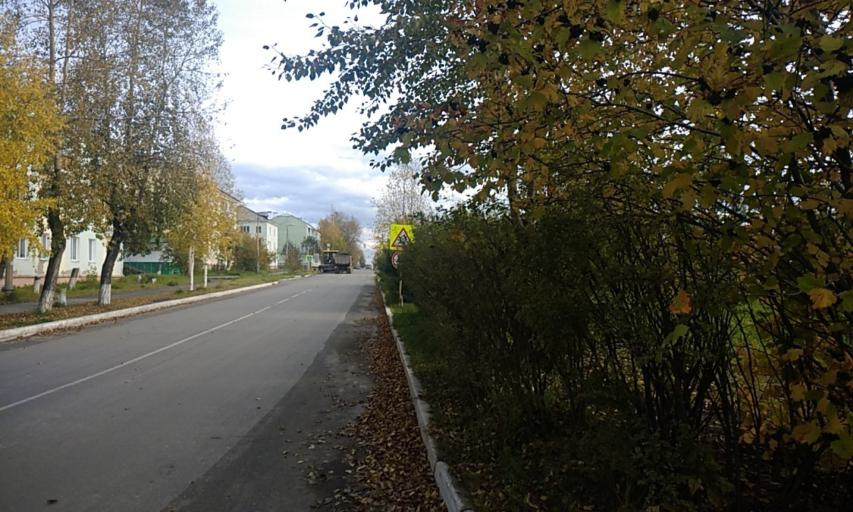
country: RU
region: Sverdlovsk
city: Krasnoural'sk
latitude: 58.3542
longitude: 60.0561
